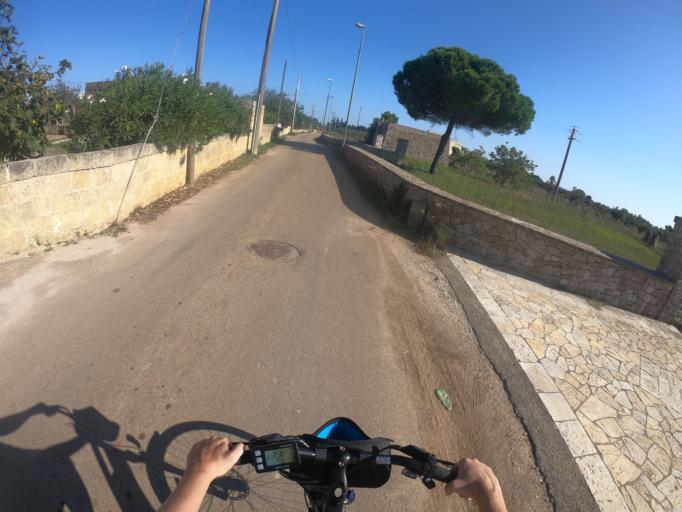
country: IT
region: Apulia
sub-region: Provincia di Lecce
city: Alessano
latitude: 39.8892
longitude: 18.3226
